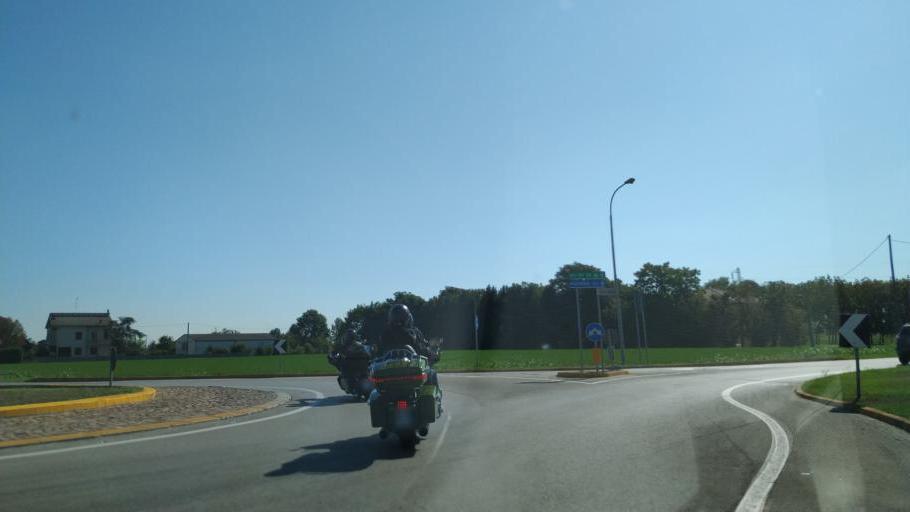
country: IT
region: Emilia-Romagna
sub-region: Provincia di Ferrara
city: San Carlo
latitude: 44.8019
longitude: 11.4152
